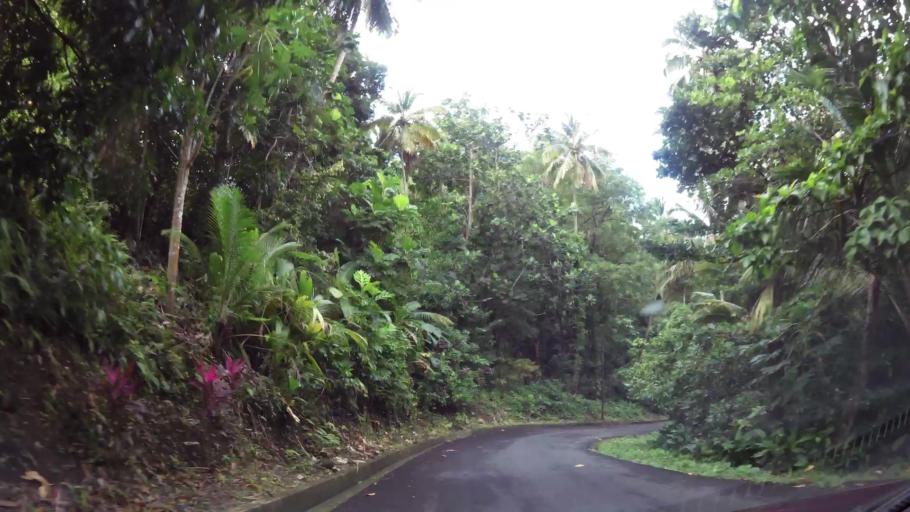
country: DM
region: Saint John
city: Portsmouth
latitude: 15.6213
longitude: -61.4595
